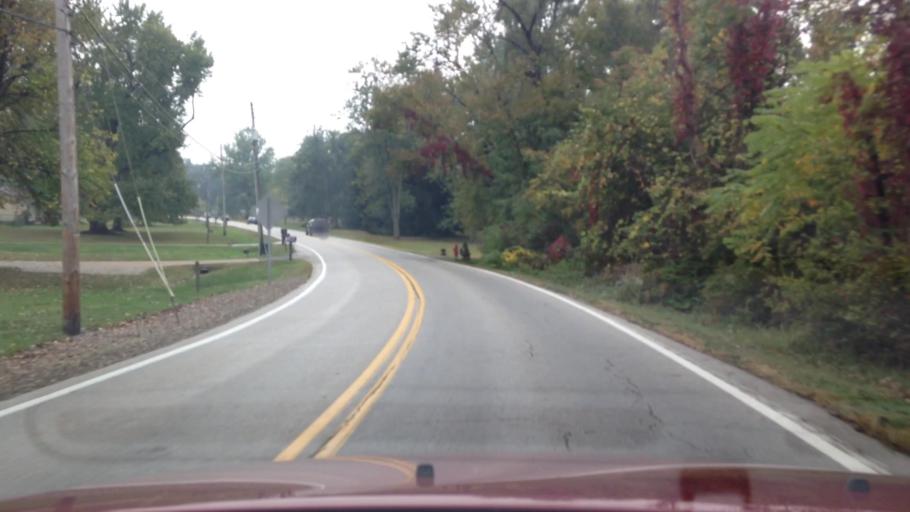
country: US
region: Ohio
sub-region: Cuyahoga County
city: Walton Hills
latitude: 41.3501
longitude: -81.5620
